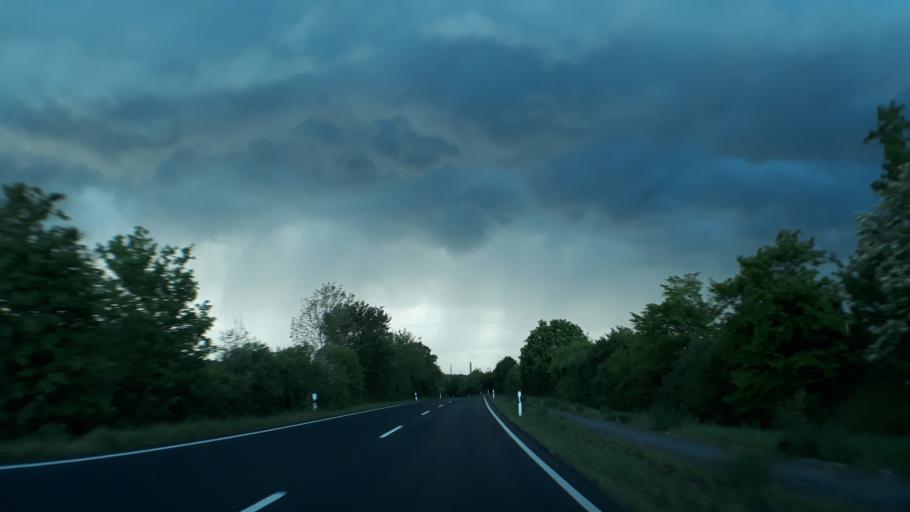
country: DE
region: North Rhine-Westphalia
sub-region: Regierungsbezirk Koln
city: Langerwehe
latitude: 50.8122
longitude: 6.3181
